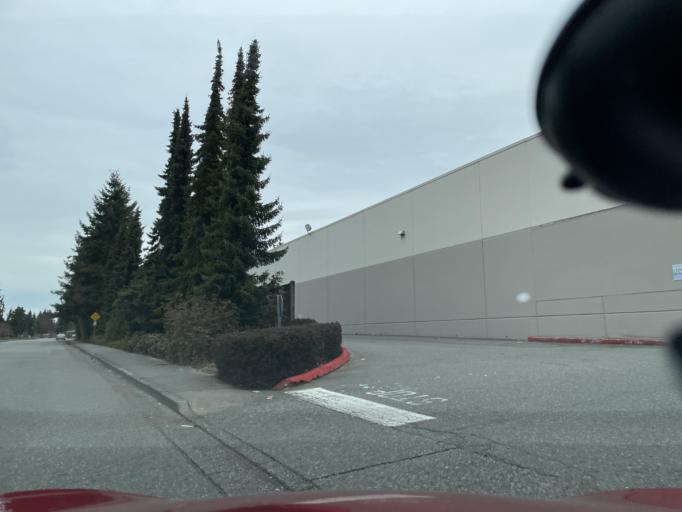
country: US
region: Washington
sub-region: Snohomish County
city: Mill Creek
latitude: 47.9100
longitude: -122.2282
